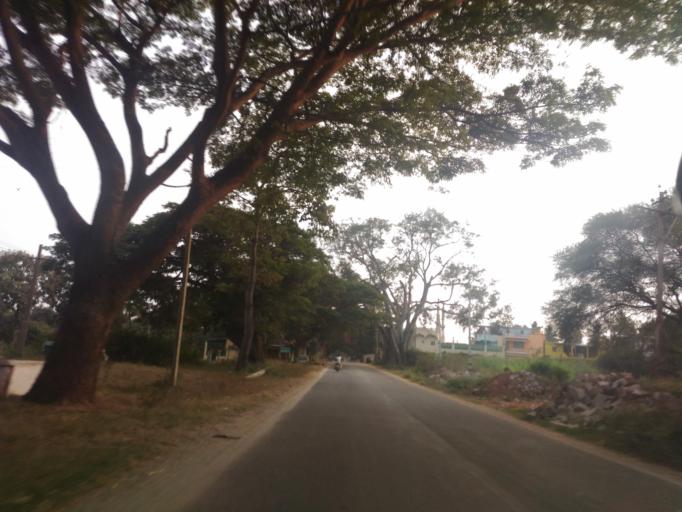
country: IN
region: Karnataka
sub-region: Bangalore Rural
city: Devanhalli
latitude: 13.3311
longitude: 77.6910
